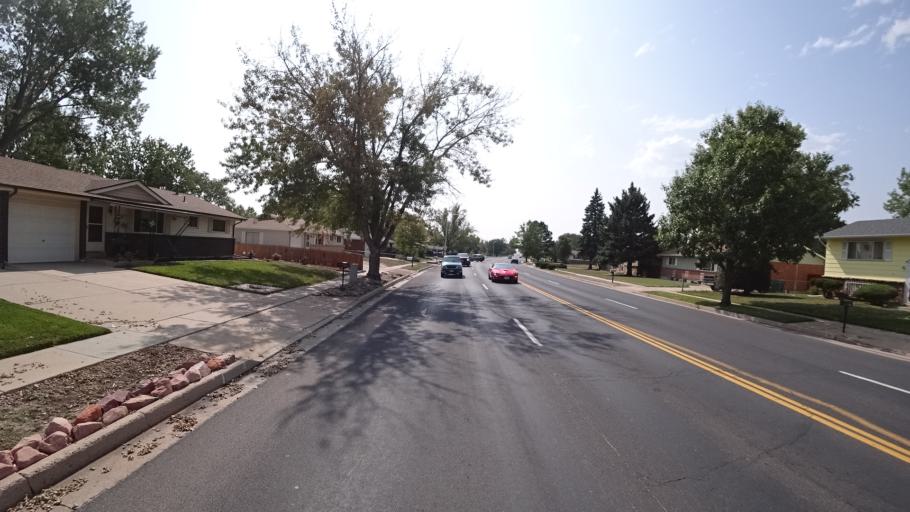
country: US
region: Colorado
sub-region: El Paso County
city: Cimarron Hills
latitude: 38.8530
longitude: -104.7479
